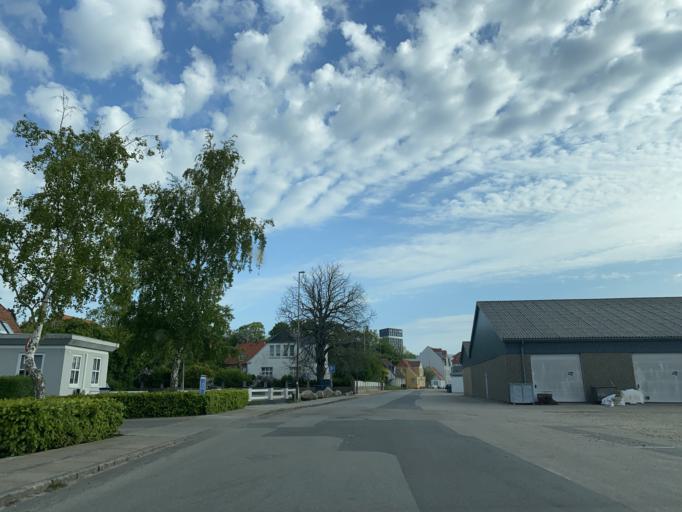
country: DK
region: South Denmark
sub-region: Sonderborg Kommune
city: Sonderborg
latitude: 54.9084
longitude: 9.7802
